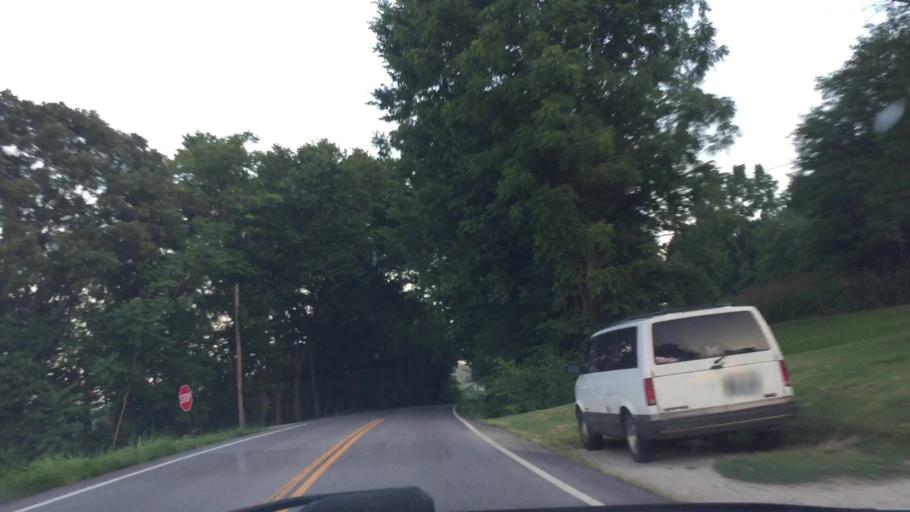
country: US
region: Kentucky
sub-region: Carroll County
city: Carrollton
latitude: 38.6382
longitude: -85.1407
